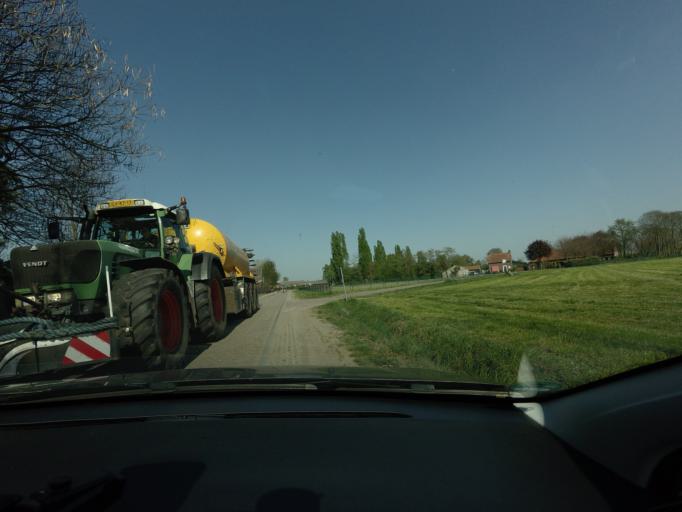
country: NL
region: North Brabant
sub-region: Gemeente Baarle-Nassau
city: Baarle-Nassau
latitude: 51.4816
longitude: 4.9747
